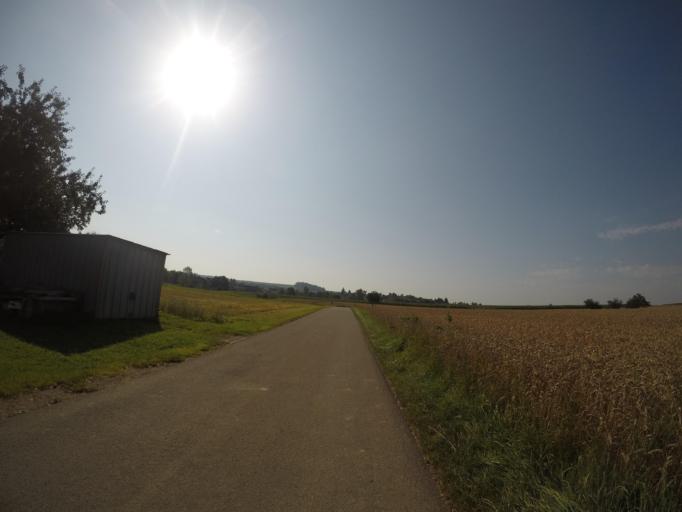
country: DE
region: Baden-Wuerttemberg
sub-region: Tuebingen Region
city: Wain
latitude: 48.1978
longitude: 10.0179
